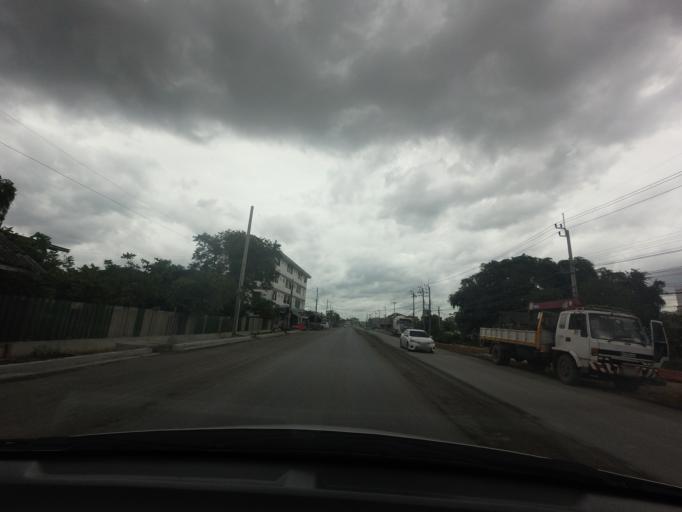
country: TH
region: Bangkok
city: Lat Krabang
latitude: 13.7612
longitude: 100.7762
